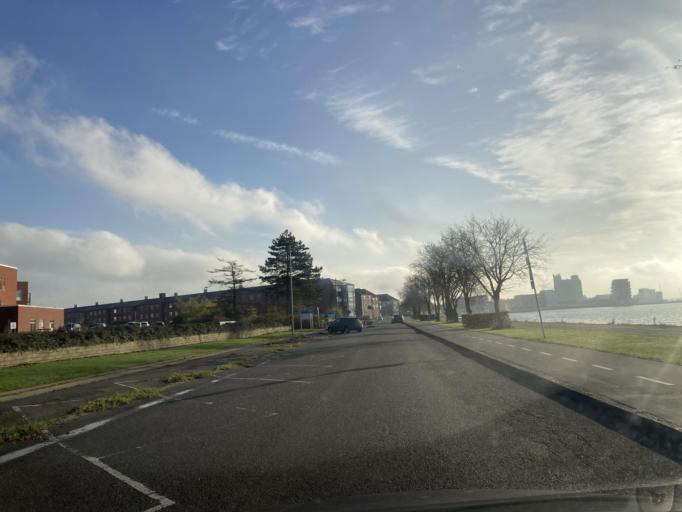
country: DK
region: Zealand
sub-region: Guldborgsund Kommune
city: Nykobing Falster
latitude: 54.7781
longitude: 11.8573
